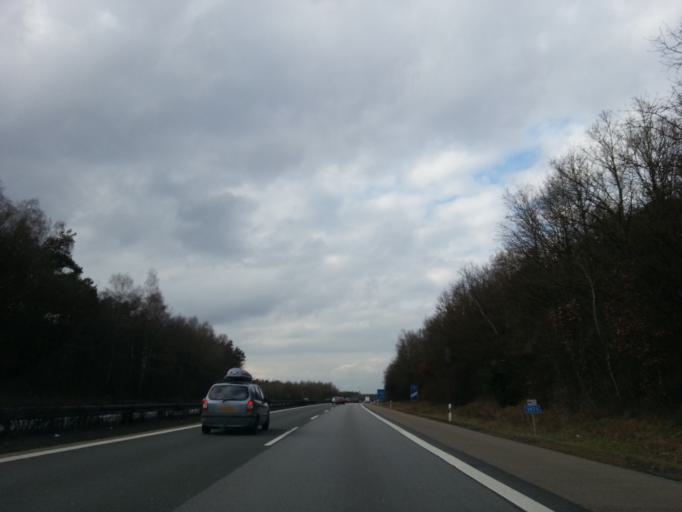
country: DE
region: Bavaria
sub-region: Regierungsbezirk Mittelfranken
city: Hochstadt an der Aisch
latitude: 49.7232
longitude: 10.8270
